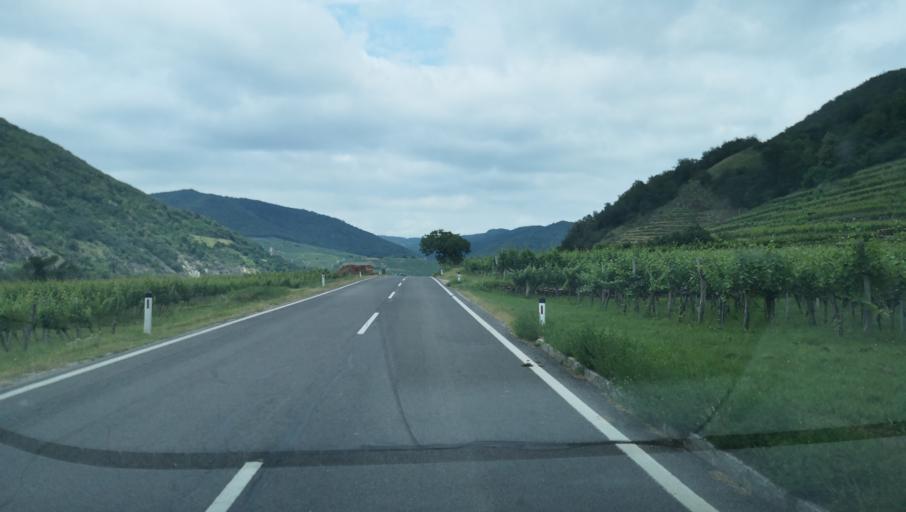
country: AT
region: Lower Austria
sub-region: Politischer Bezirk Krems
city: Spitz
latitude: 48.3425
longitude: 15.4112
